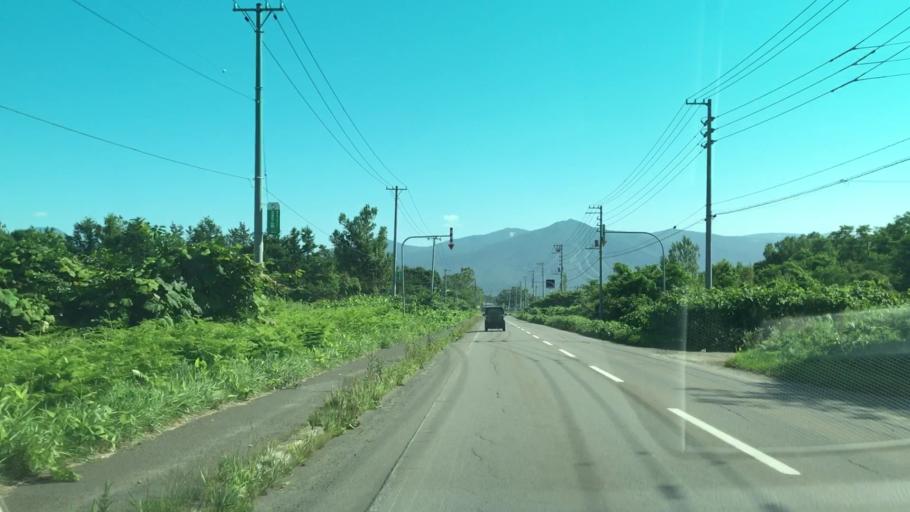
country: JP
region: Hokkaido
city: Iwanai
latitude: 43.0109
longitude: 140.5434
